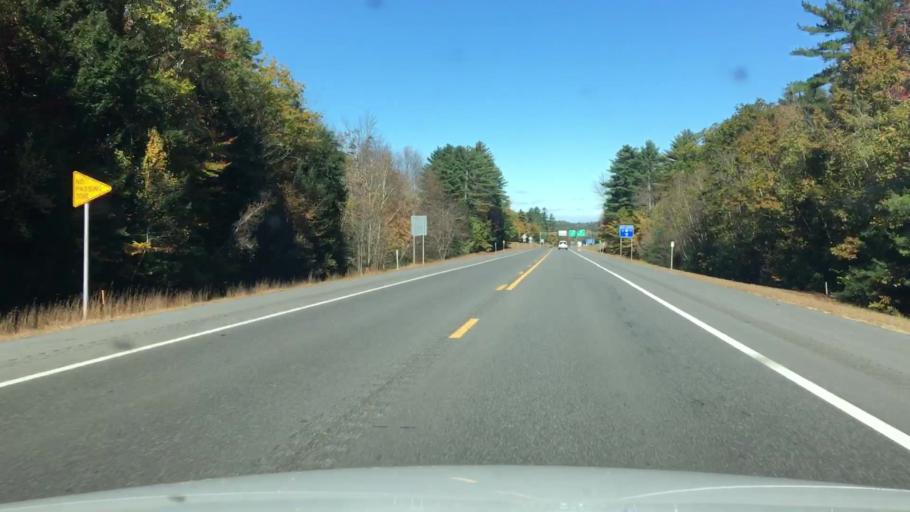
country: US
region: New Hampshire
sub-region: Carroll County
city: Sanbornville
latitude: 43.4712
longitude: -71.0007
